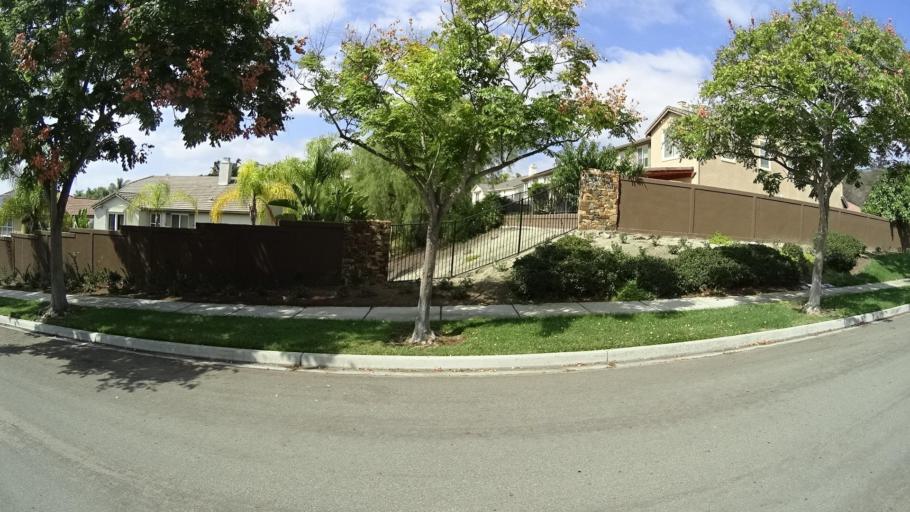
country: US
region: California
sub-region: San Diego County
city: Fairbanks Ranch
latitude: 33.0068
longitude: -117.1058
